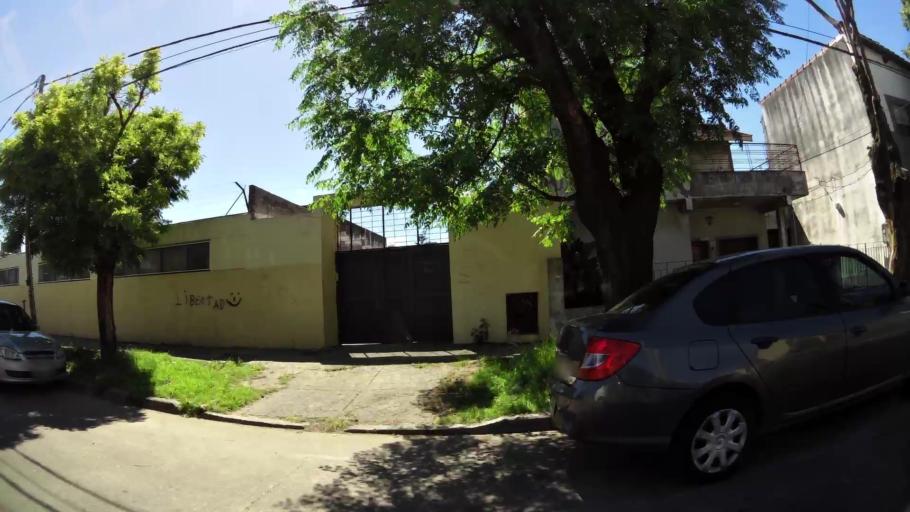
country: AR
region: Buenos Aires
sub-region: Partido de General San Martin
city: General San Martin
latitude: -34.5308
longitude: -58.5645
